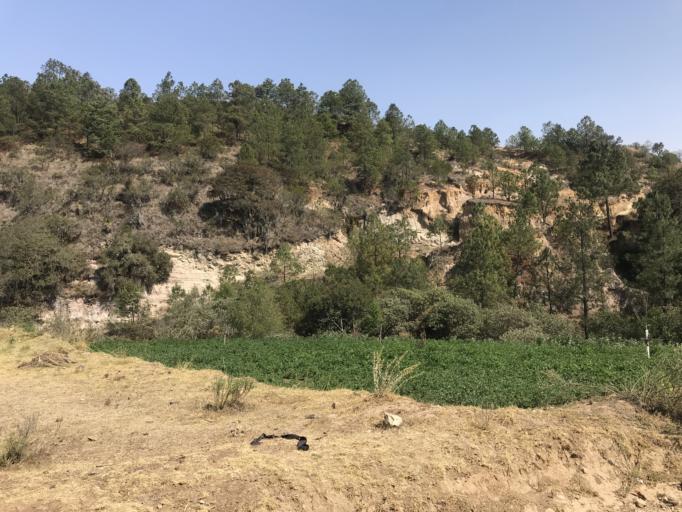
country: MX
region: Puebla
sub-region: Zautla
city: San Andres Yahuitlalpan
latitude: 19.7023
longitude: -97.8378
